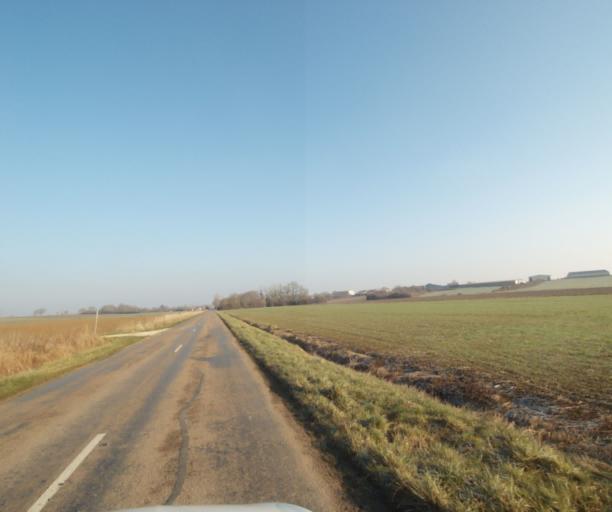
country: FR
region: Champagne-Ardenne
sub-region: Departement de la Haute-Marne
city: Montier-en-Der
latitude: 48.4470
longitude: 4.7622
